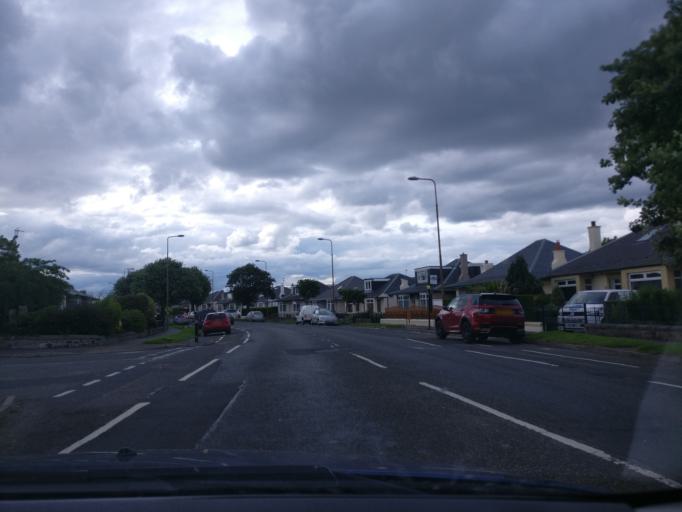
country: GB
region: Scotland
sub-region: West Lothian
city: Seafield
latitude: 55.9601
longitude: -3.1277
